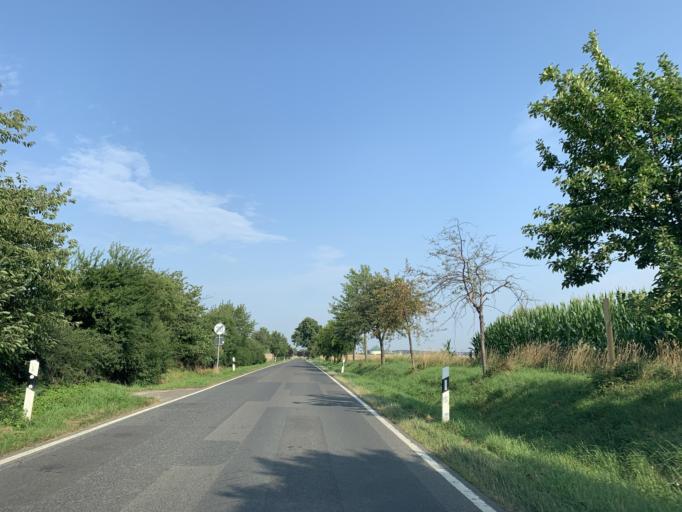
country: DE
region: Mecklenburg-Vorpommern
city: Blankensee
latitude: 53.4145
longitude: 13.2228
